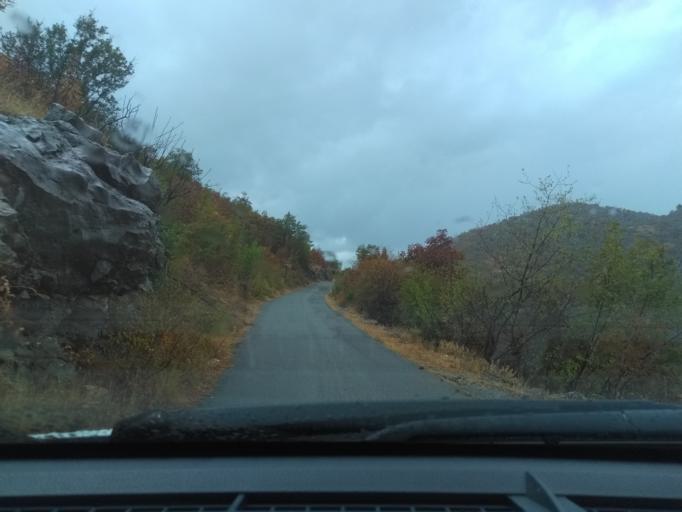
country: ME
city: Stari Bar
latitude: 42.1836
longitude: 19.1735
